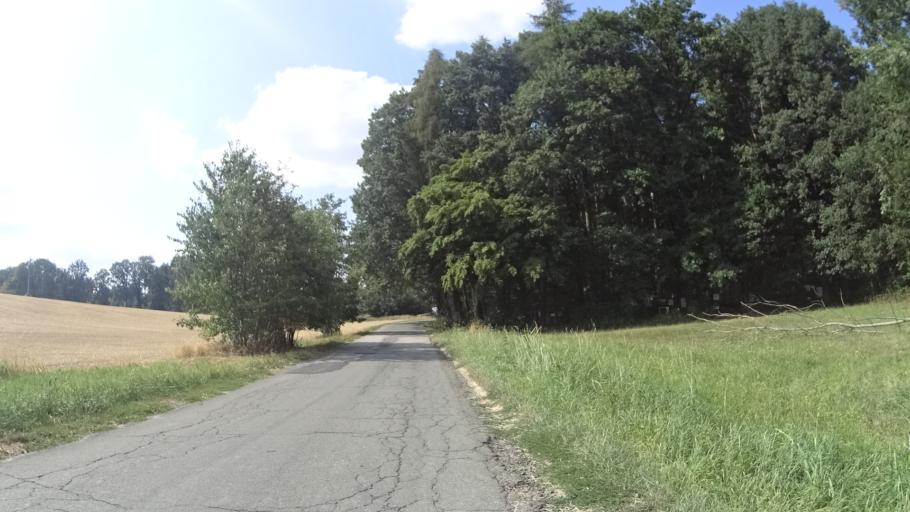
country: CZ
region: Kralovehradecky
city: Liban
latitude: 50.4276
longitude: 15.2592
